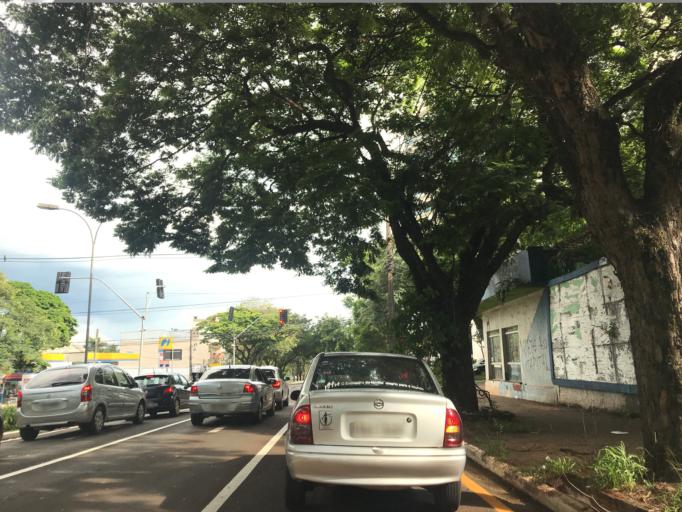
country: BR
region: Parana
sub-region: Maringa
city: Maringa
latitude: -23.4331
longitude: -51.9290
